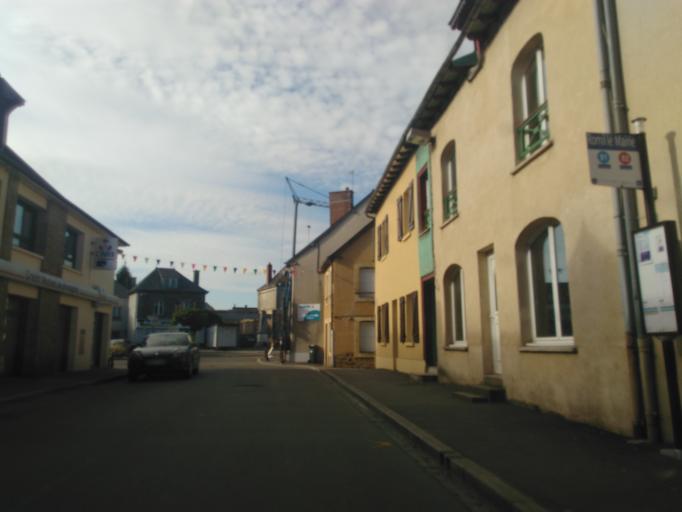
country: FR
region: Brittany
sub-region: Departement d'Ille-et-Vilaine
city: Romille
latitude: 48.2148
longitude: -1.8924
